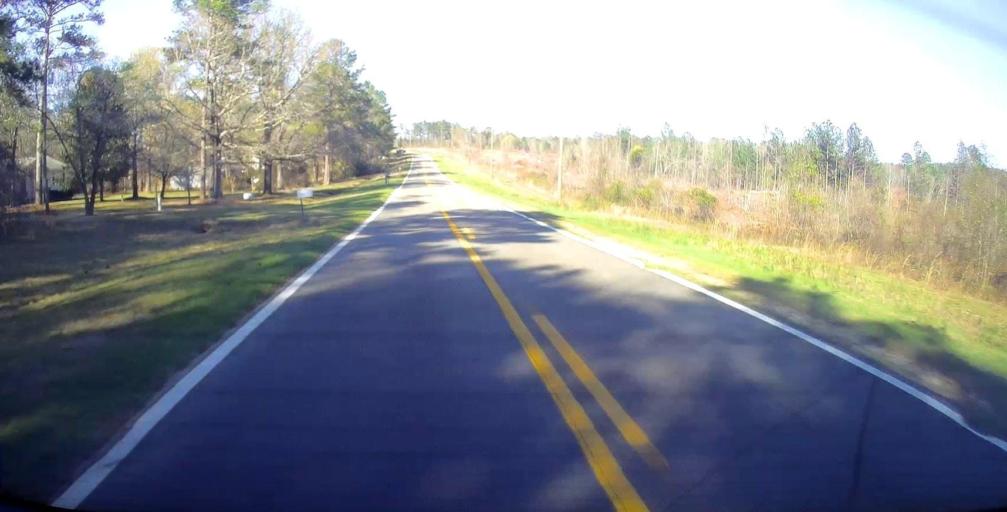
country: US
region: Georgia
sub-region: Taylor County
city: Reynolds
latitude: 32.5805
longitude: -83.9924
